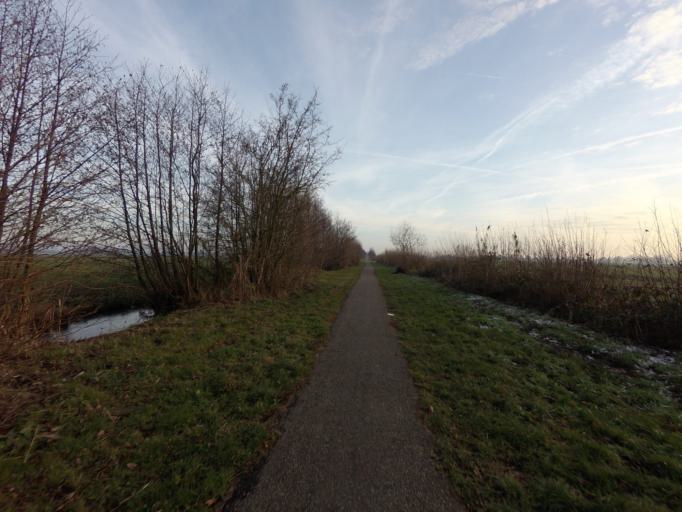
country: NL
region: Utrecht
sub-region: Gemeente Woerden
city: Woerden
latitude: 52.1449
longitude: 4.9265
